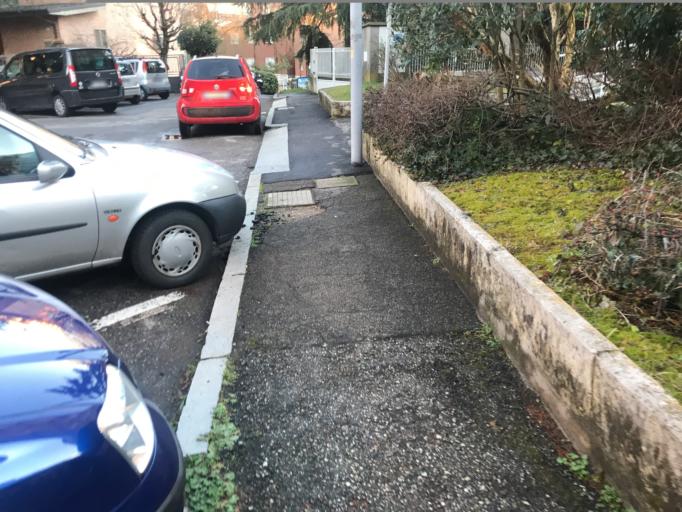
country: IT
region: Emilia-Romagna
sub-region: Provincia di Bologna
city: Progresso
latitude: 44.5434
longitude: 11.3533
